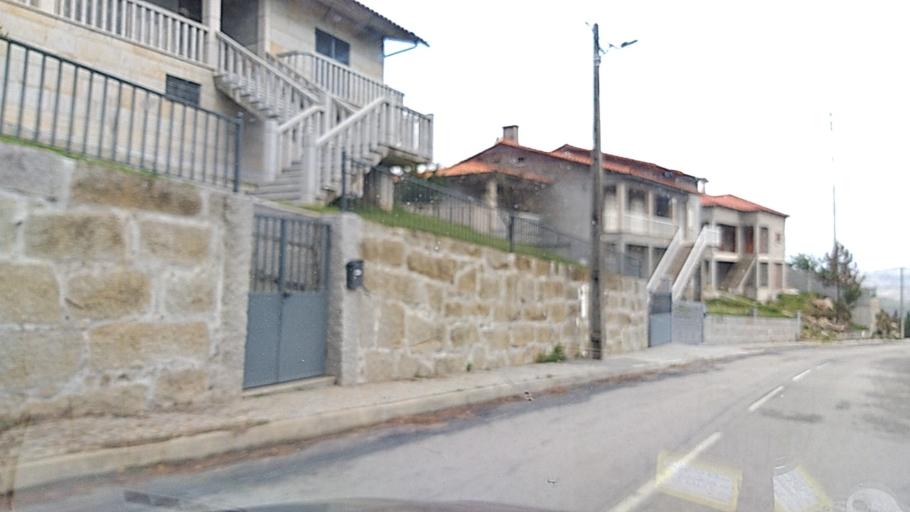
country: PT
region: Guarda
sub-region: Fornos de Algodres
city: Fornos de Algodres
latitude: 40.6663
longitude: -7.6105
